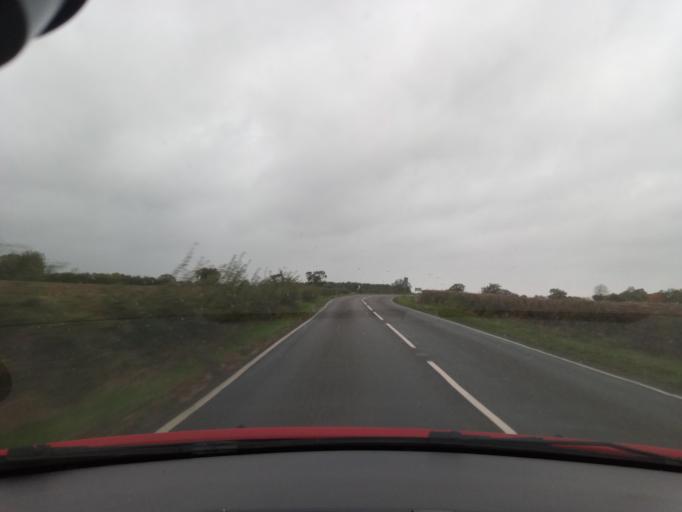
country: GB
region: England
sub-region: Essex
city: Great Yeldham
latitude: 52.0420
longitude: 0.5250
